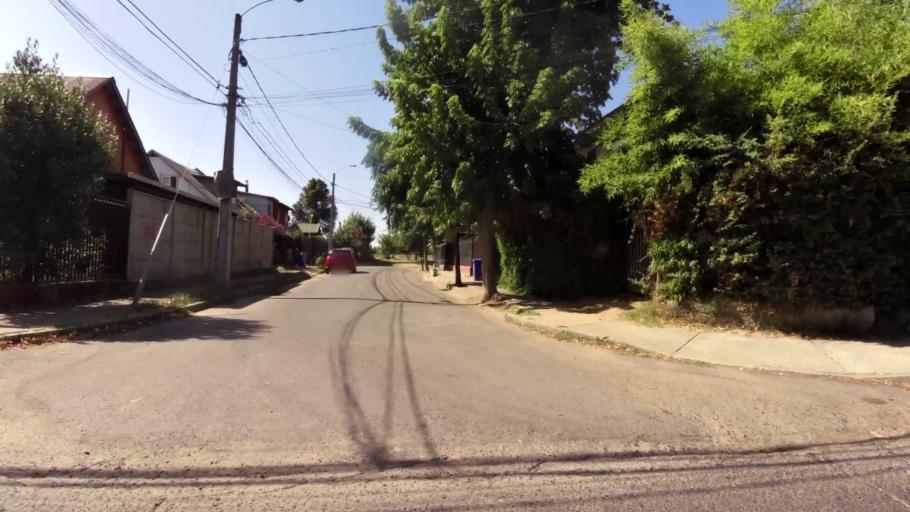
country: CL
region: Maule
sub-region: Provincia de Talca
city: Talca
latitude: -35.4108
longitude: -71.6366
